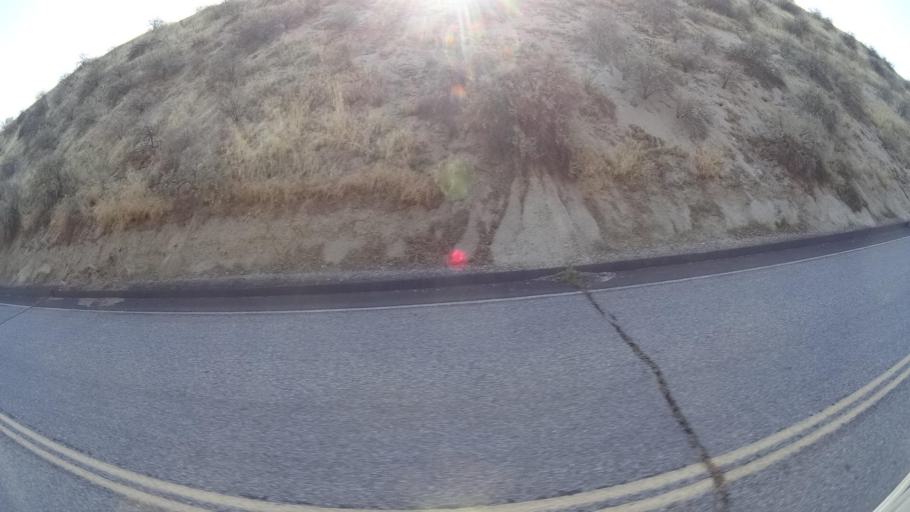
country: US
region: California
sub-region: Kern County
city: Oildale
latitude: 35.5271
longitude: -118.9754
